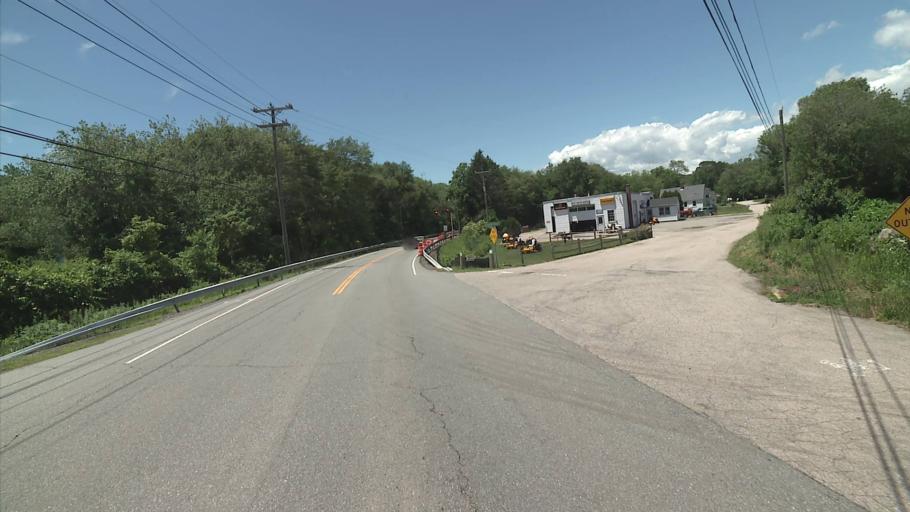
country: US
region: Connecticut
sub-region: New London County
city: Pawcatuck
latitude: 41.3823
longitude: -71.8727
